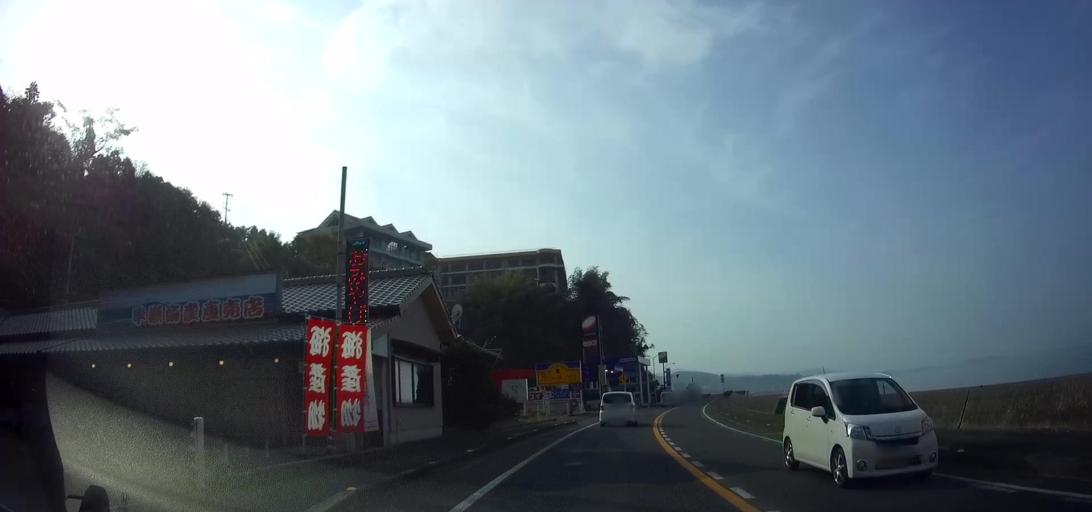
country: JP
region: Nagasaki
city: Shimabara
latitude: 32.7377
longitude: 130.2100
